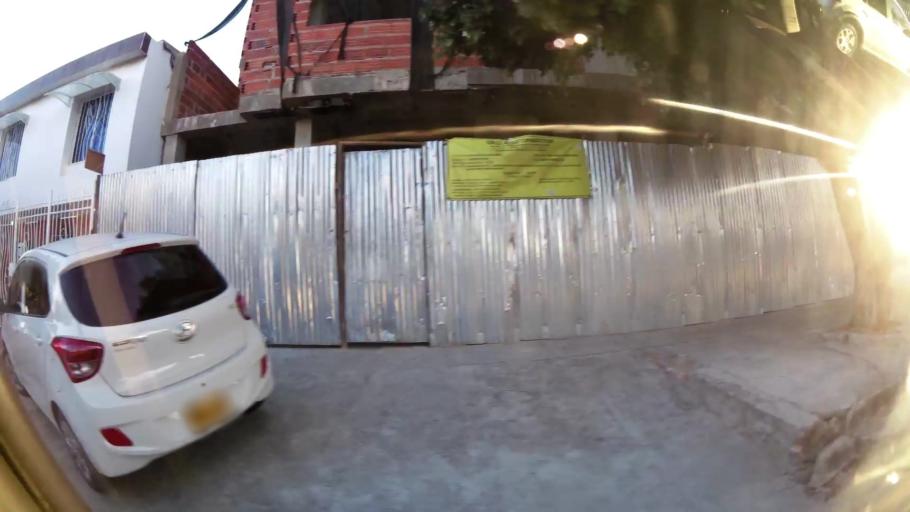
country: CO
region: Atlantico
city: Barranquilla
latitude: 10.9728
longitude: -74.8031
